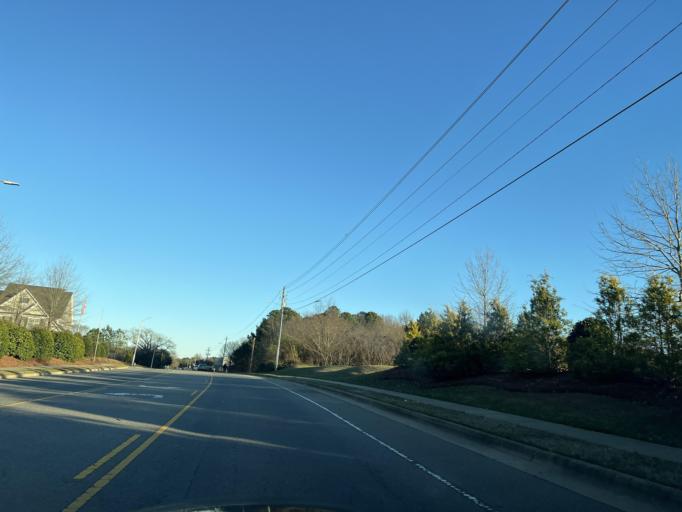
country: US
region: North Carolina
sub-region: Wake County
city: Fuquay-Varina
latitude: 35.5740
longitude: -78.8063
